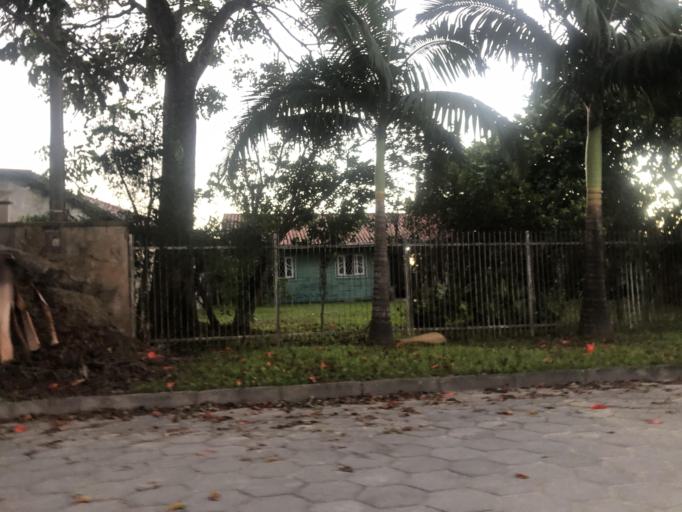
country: BR
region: Santa Catarina
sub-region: Sao Francisco Do Sul
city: Sao Francisco do Sul
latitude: -26.2127
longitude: -48.5294
